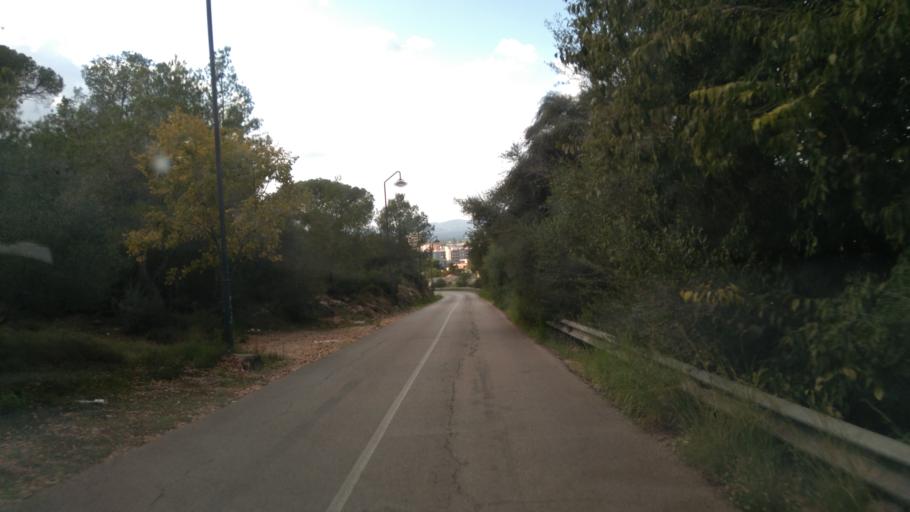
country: ES
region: Valencia
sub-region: Provincia de Valencia
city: Alzira
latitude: 39.1540
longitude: -0.4196
